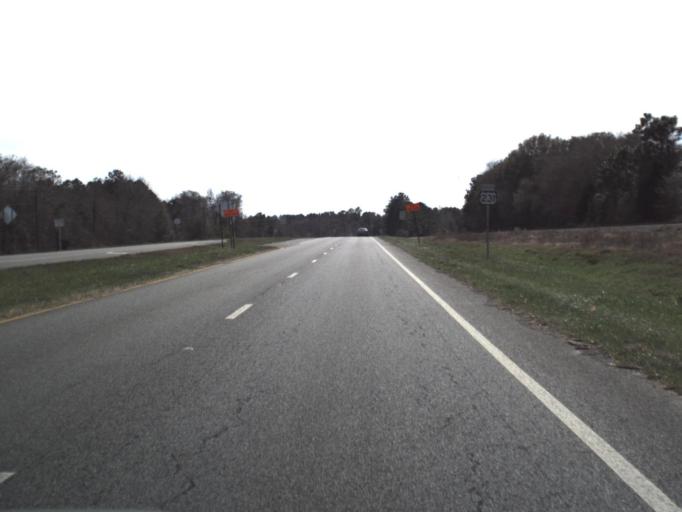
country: US
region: Florida
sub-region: Washington County
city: Chipley
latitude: 30.6667
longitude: -85.3933
